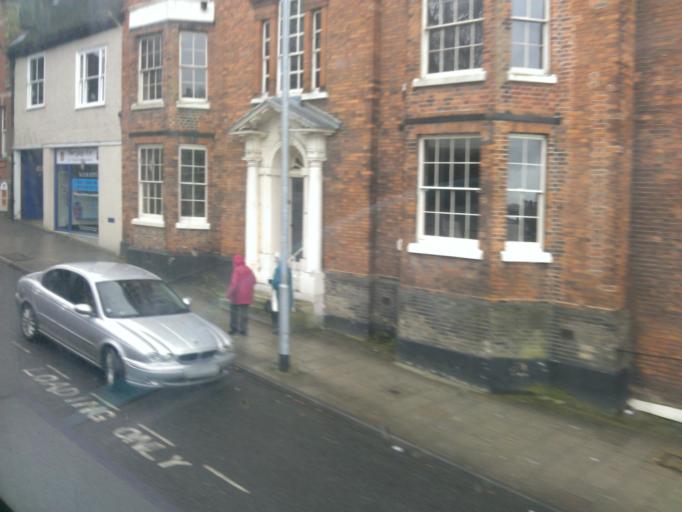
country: GB
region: England
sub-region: Essex
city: Colchester
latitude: 51.8905
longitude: 0.8964
